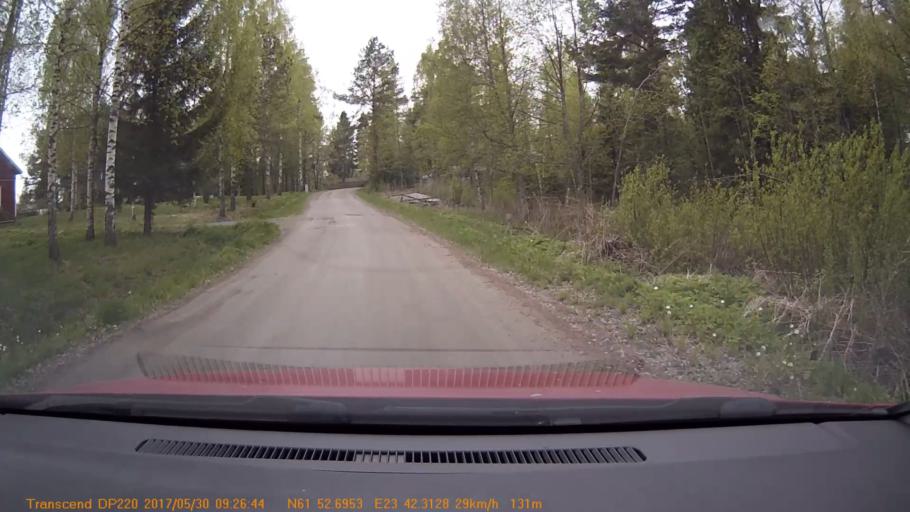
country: FI
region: Pirkanmaa
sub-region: Tampere
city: Kuru
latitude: 61.8783
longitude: 23.7052
